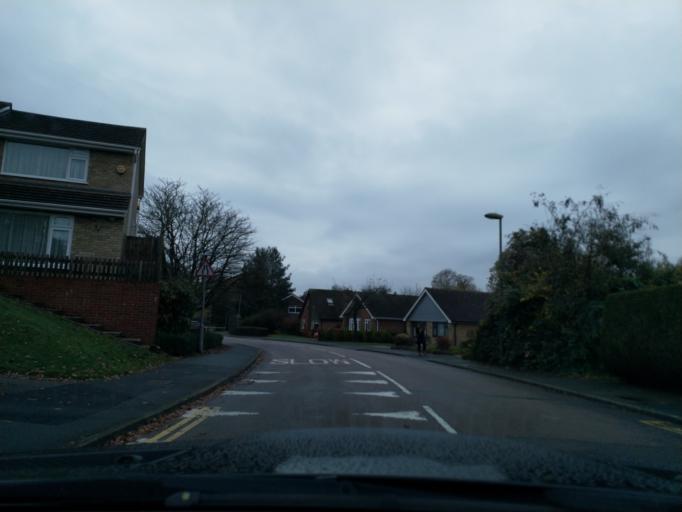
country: GB
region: England
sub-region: Surrey
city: Frimley
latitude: 51.3187
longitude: -0.7285
